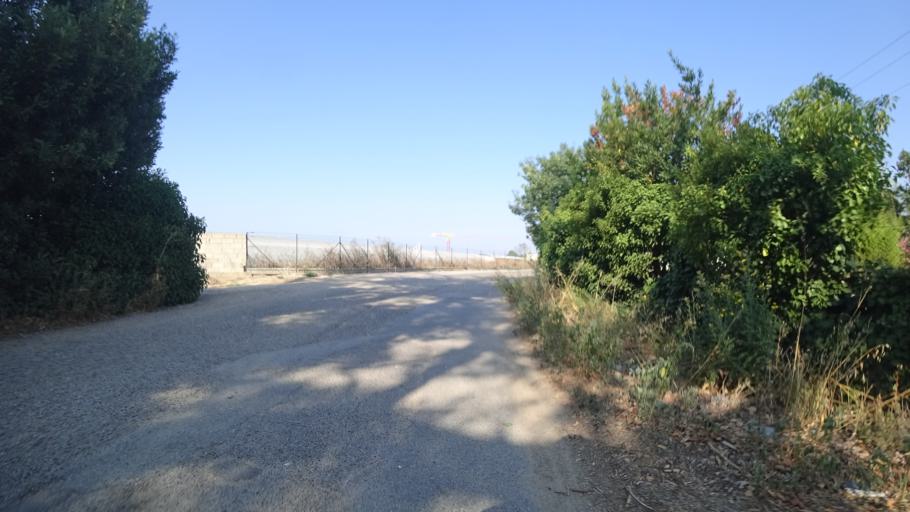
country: FR
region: Languedoc-Roussillon
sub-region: Departement des Pyrenees-Orientales
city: Perpignan
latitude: 42.7020
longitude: 2.8715
